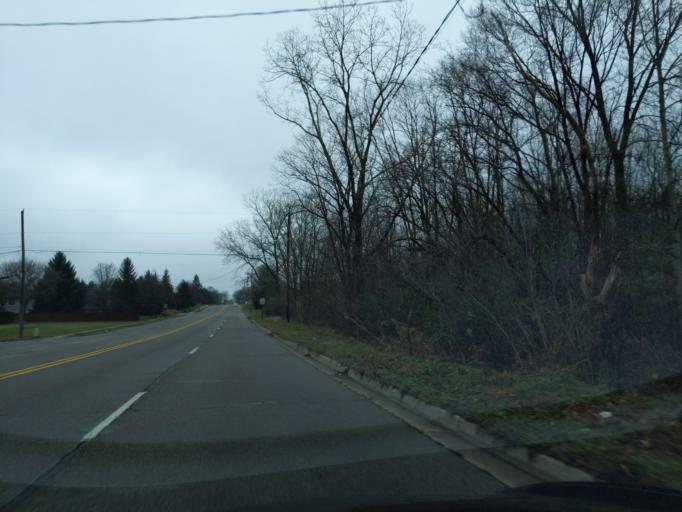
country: US
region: Michigan
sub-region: Jackson County
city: Jackson
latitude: 42.2766
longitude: -84.4366
